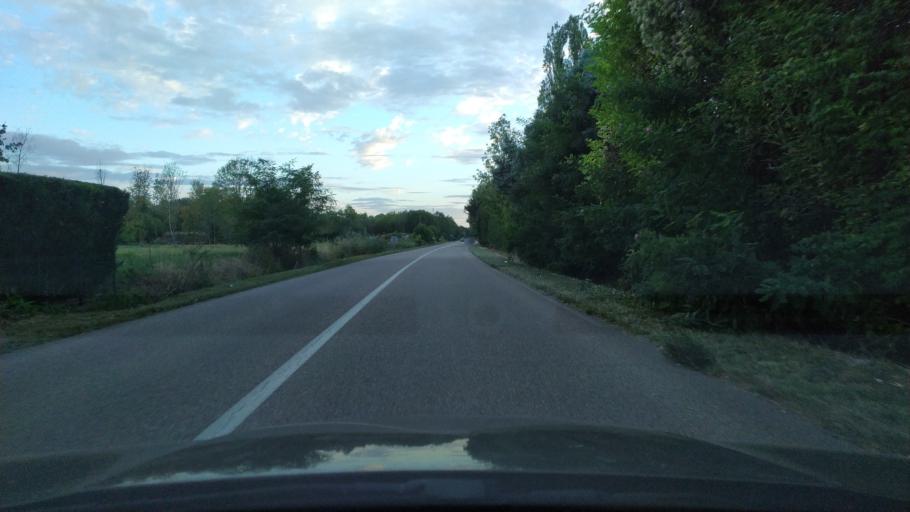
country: FR
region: Lorraine
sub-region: Departement de la Moselle
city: Moulins-les-Metz
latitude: 49.0918
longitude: 6.0941
